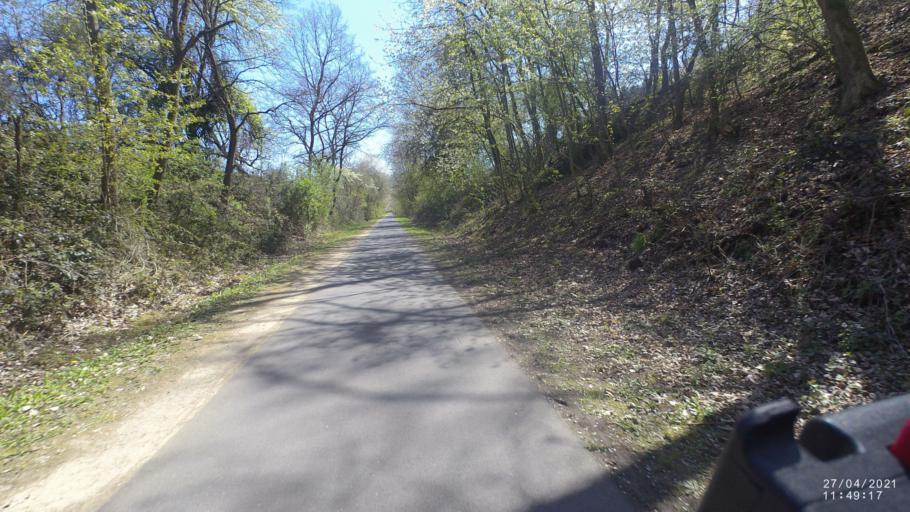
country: DE
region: Rheinland-Pfalz
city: Trimbs
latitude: 50.3182
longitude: 7.2874
